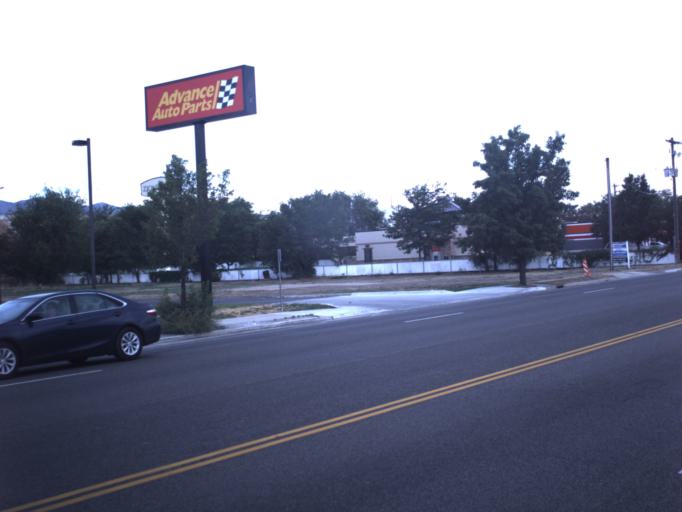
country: US
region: Utah
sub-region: Weber County
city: Roy
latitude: 41.1592
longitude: -112.0261
